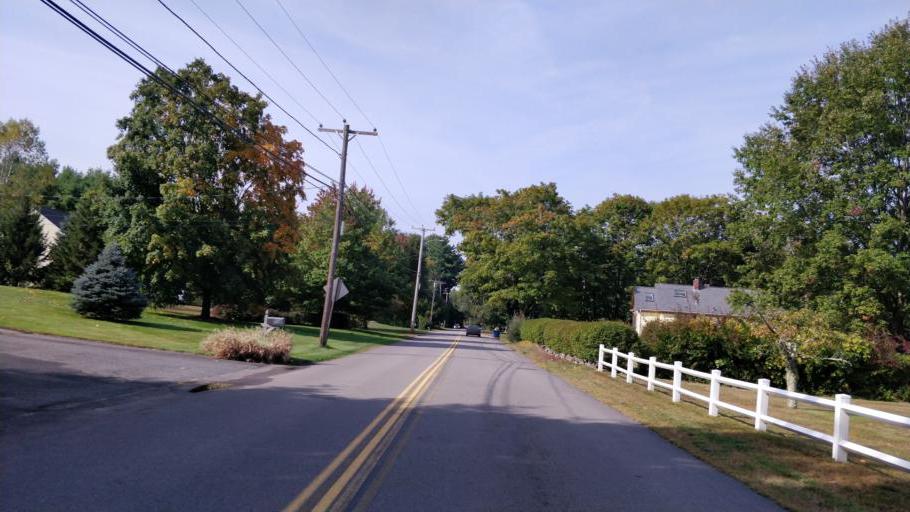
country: US
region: Massachusetts
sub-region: Bristol County
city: Norton Center
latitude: 41.9666
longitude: -71.1704
